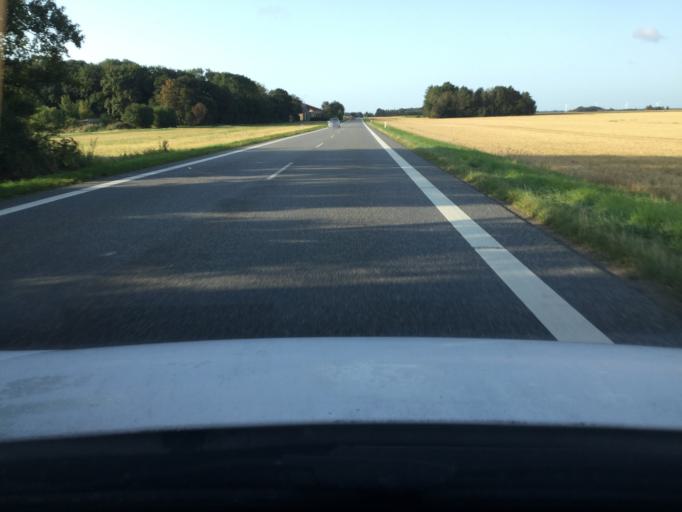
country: DK
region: Zealand
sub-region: Lolland Kommune
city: Rodby
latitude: 54.7331
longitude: 11.3892
